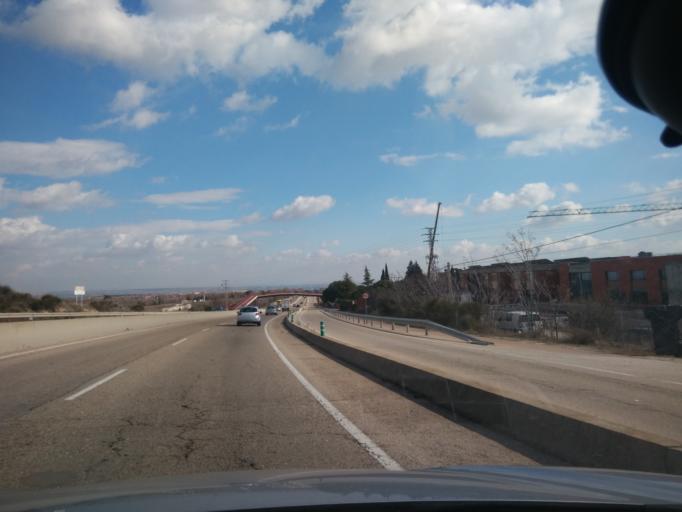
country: ES
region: Madrid
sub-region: Provincia de Madrid
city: Alcobendas
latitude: 40.5536
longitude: -3.6781
